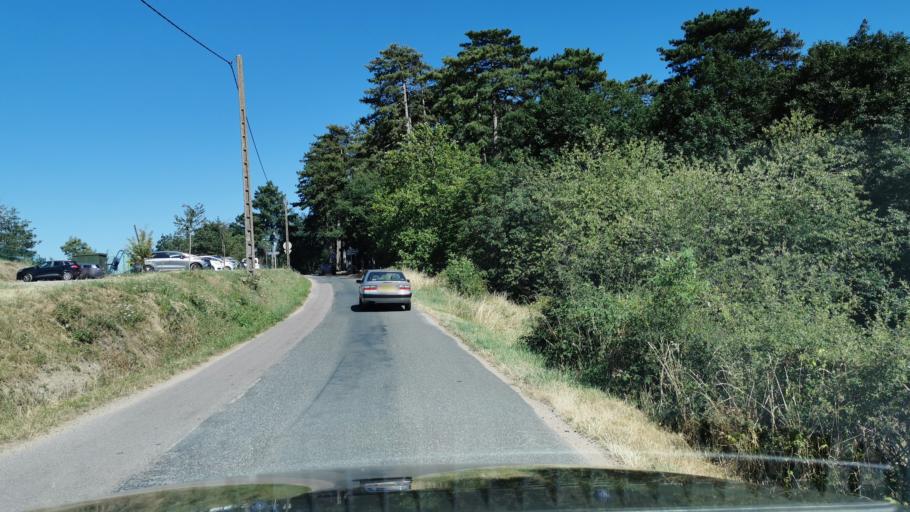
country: FR
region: Bourgogne
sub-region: Departement de Saone-et-Loire
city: Le Creusot
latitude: 46.8114
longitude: 4.4090
